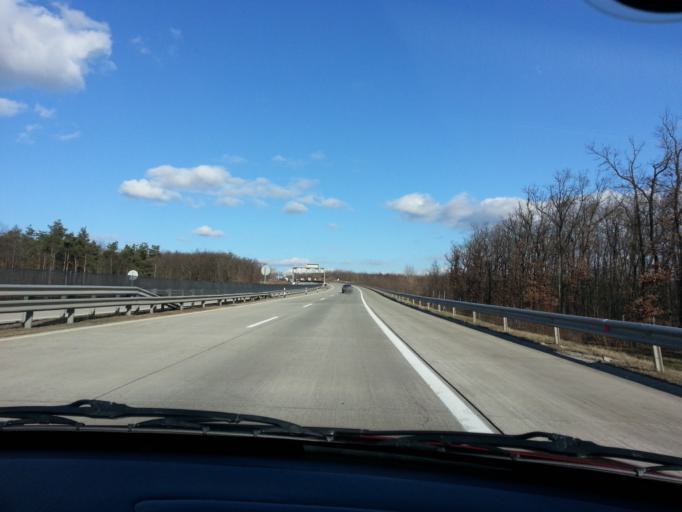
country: HU
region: Pest
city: Godollo
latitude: 47.5921
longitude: 19.3152
